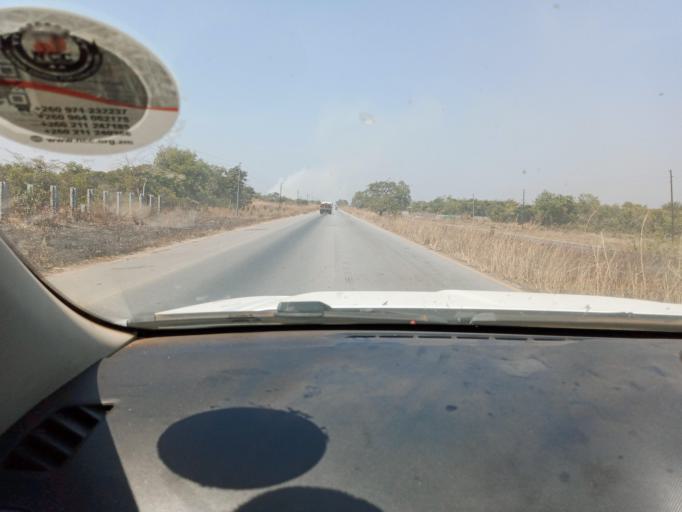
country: ZM
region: Copperbelt
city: Kitwe
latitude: -12.9136
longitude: 28.3430
